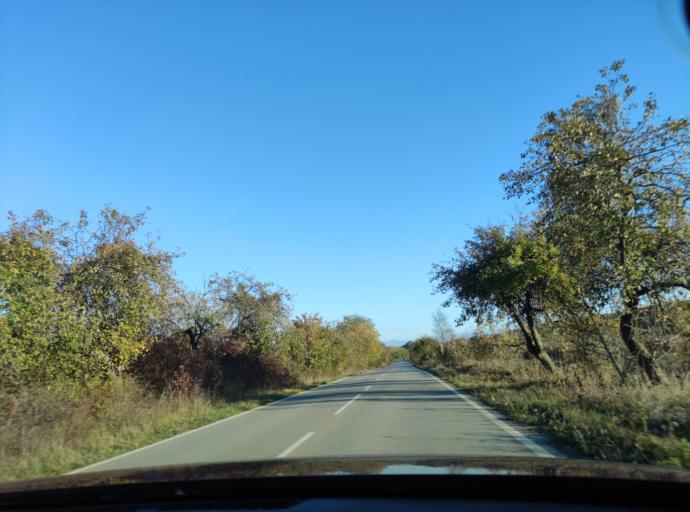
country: BG
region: Montana
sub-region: Obshtina Chiprovtsi
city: Chiprovtsi
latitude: 43.4217
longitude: 23.0174
